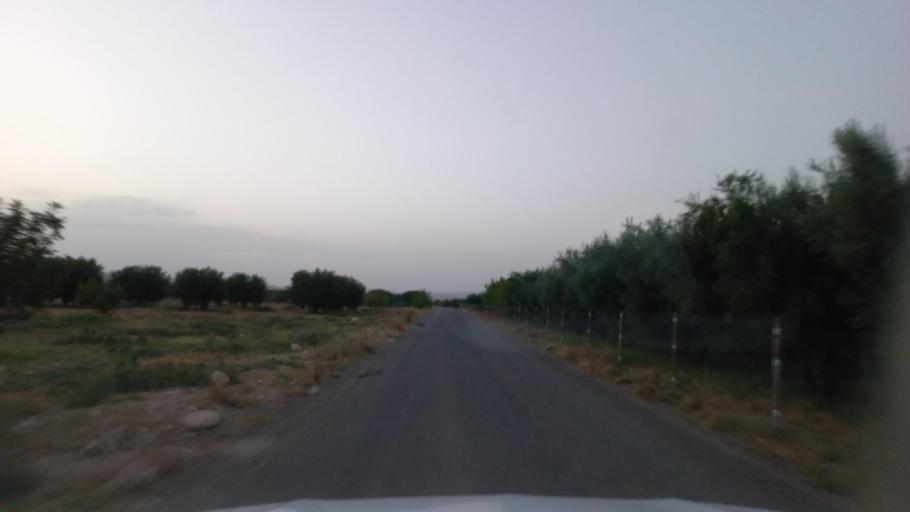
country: TN
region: Al Qasrayn
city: Kasserine
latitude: 35.2757
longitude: 9.0292
